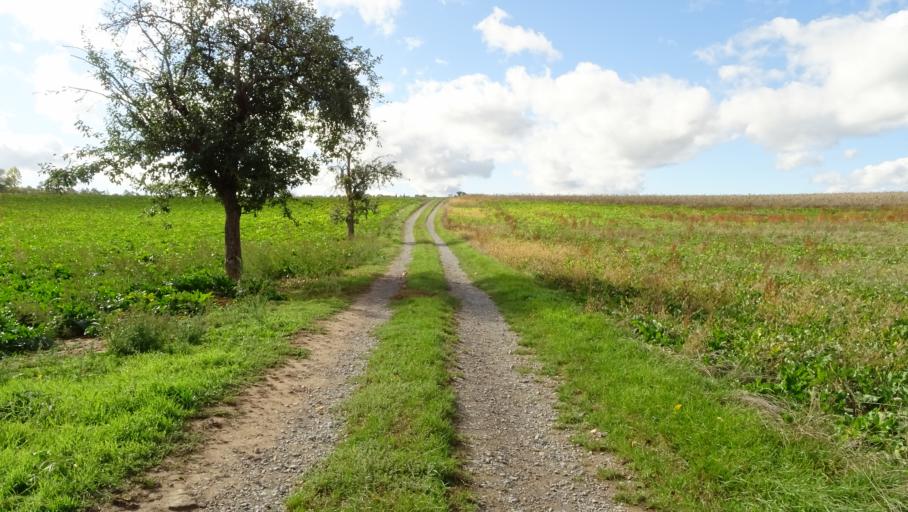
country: DE
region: Baden-Wuerttemberg
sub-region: Karlsruhe Region
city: Neckargerach
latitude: 49.3902
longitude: 9.1007
